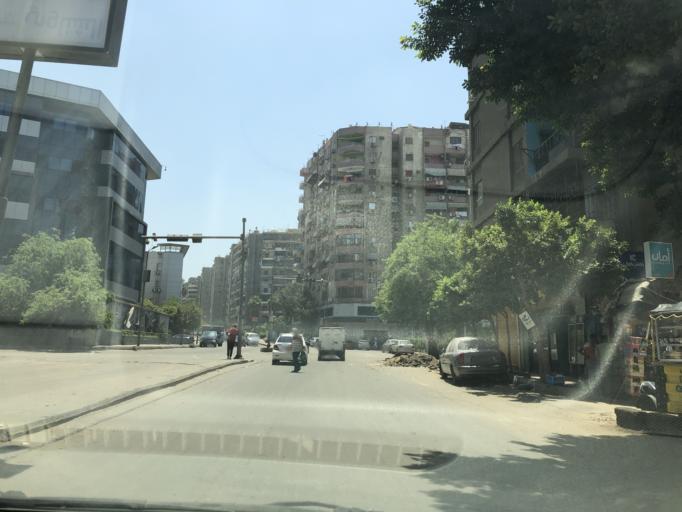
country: EG
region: Muhafazat al Qahirah
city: Cairo
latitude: 30.0629
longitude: 31.2734
